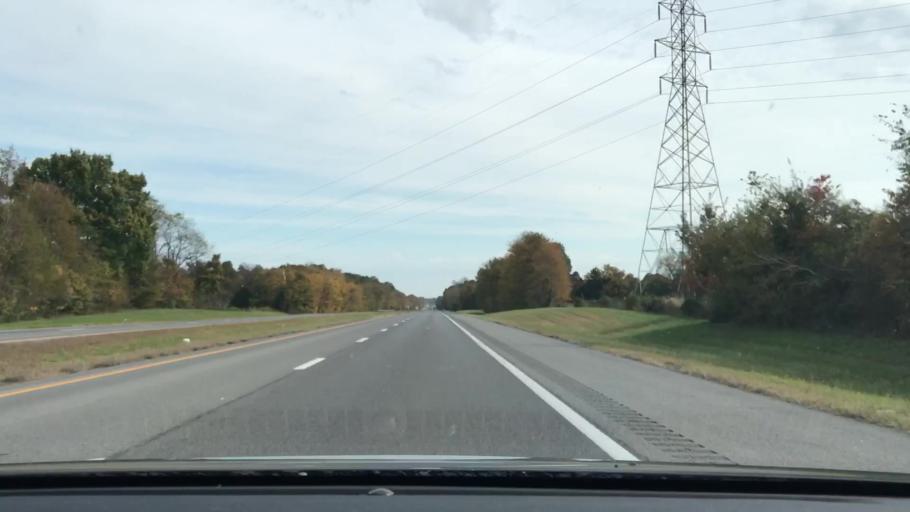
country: US
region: Kentucky
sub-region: Marshall County
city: Benton
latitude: 36.8279
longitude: -88.4561
